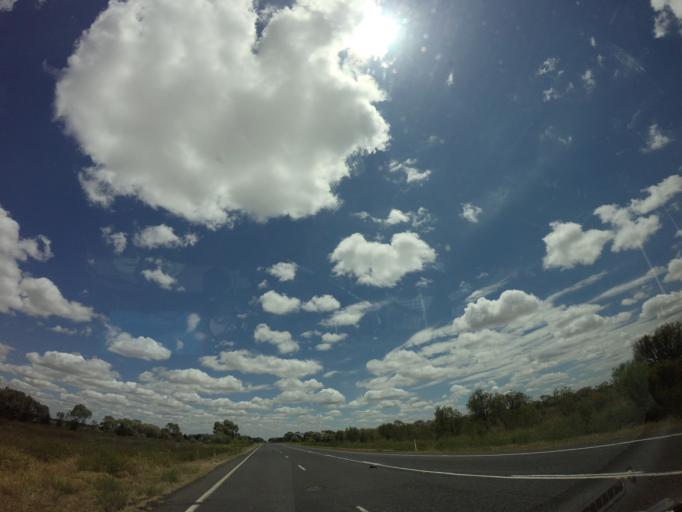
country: AU
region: New South Wales
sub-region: Moree Plains
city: Boggabilla
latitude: -28.9859
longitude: 150.0775
